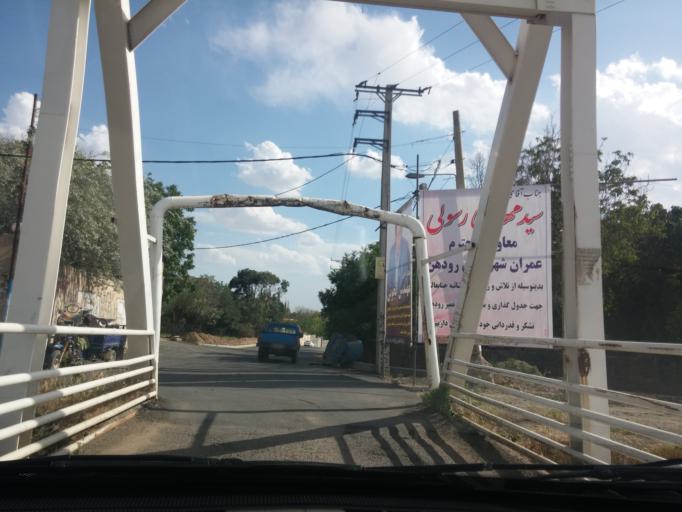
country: IR
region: Tehran
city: Damavand
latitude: 35.7251
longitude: 51.9013
